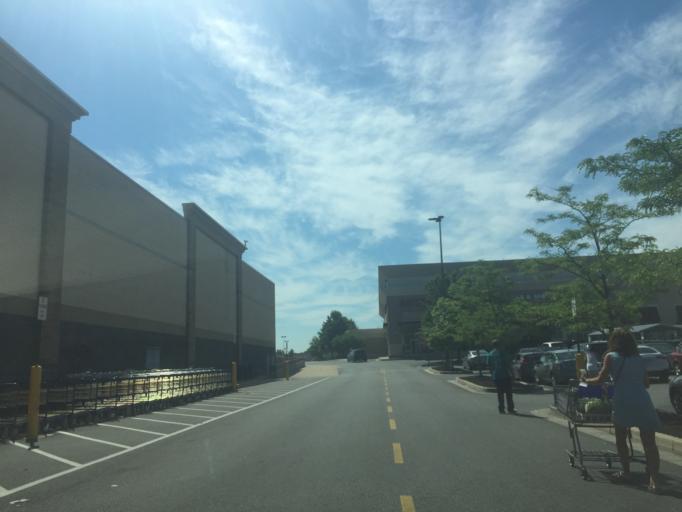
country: US
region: Maryland
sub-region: Baltimore County
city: Rossville
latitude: 39.3362
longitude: -76.4874
